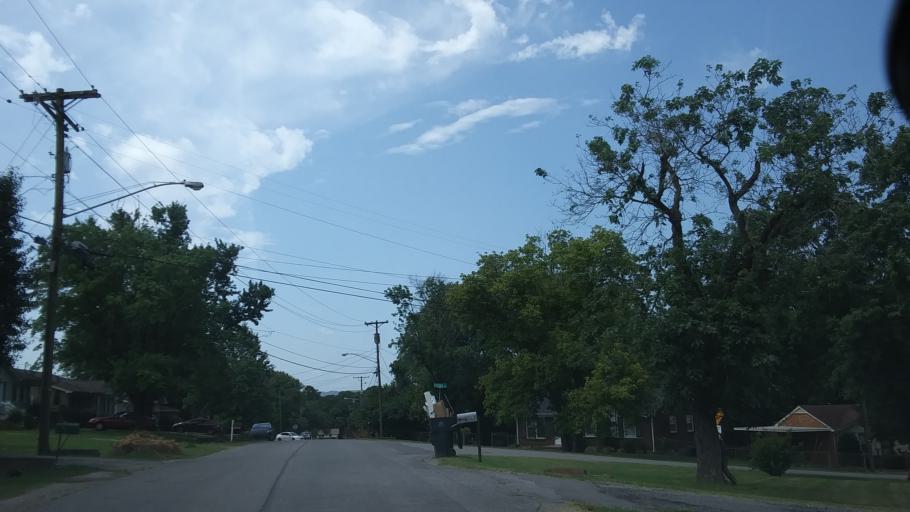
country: US
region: Tennessee
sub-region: Davidson County
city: Belle Meade
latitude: 36.1569
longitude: -86.8811
